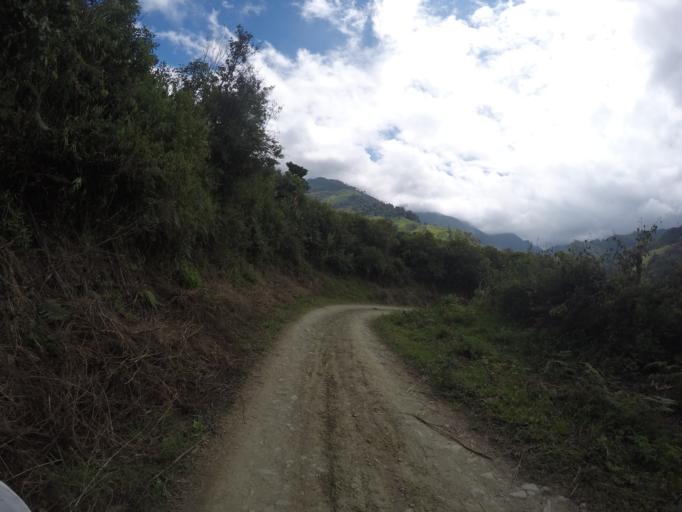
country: CO
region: Tolima
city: Cajamarca
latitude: 4.5305
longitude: -75.4133
